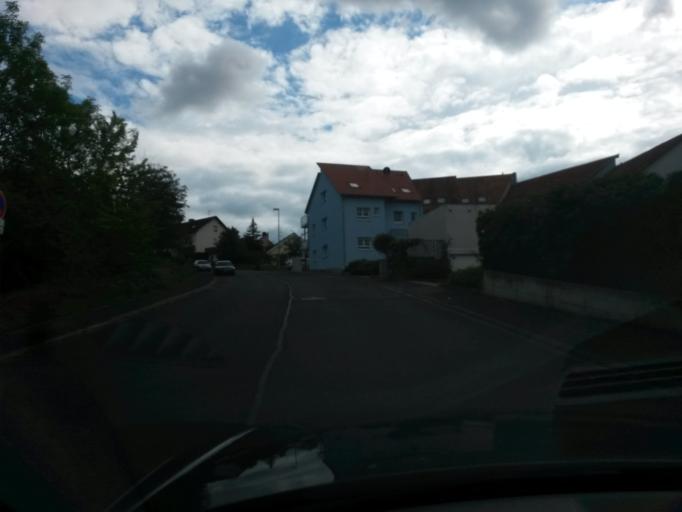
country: DE
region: Bavaria
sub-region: Regierungsbezirk Unterfranken
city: Rimpar
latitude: 49.8498
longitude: 9.9584
